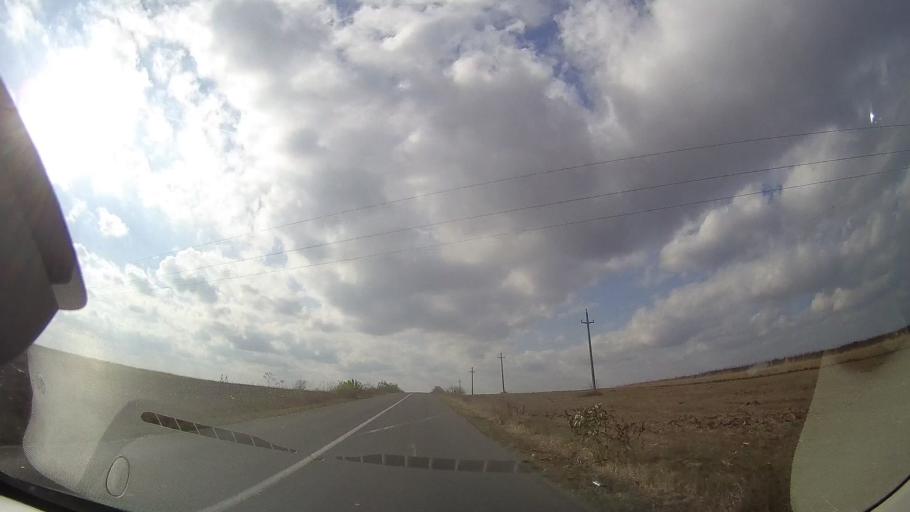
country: RO
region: Constanta
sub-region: Comuna Douazeci si Trei August
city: Dulcesti
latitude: 43.9021
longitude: 28.5376
